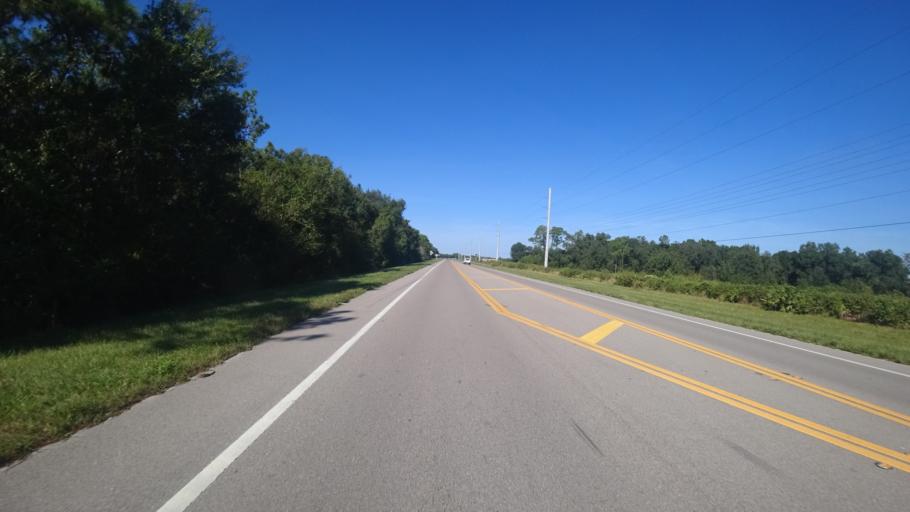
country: US
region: Florida
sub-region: Sarasota County
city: The Meadows
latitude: 27.4166
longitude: -82.3566
